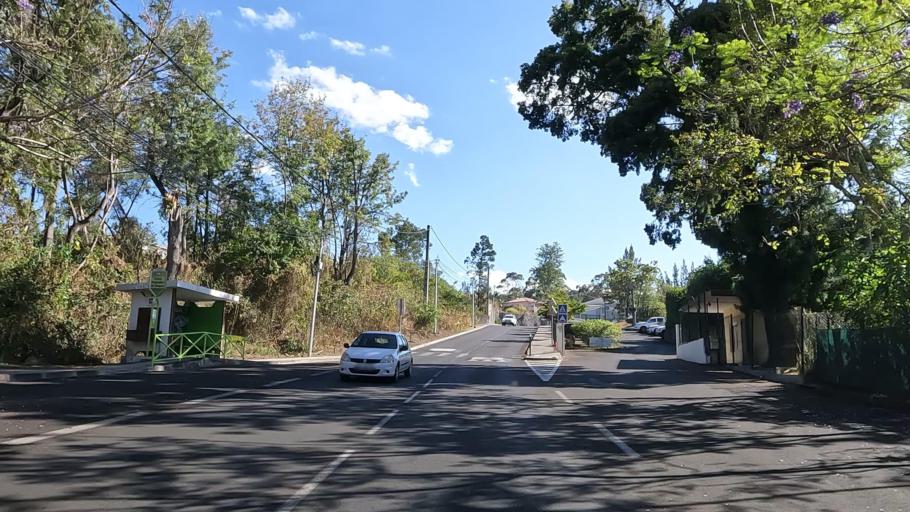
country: RE
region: Reunion
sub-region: Reunion
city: Le Tampon
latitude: -21.2599
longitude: 55.5100
